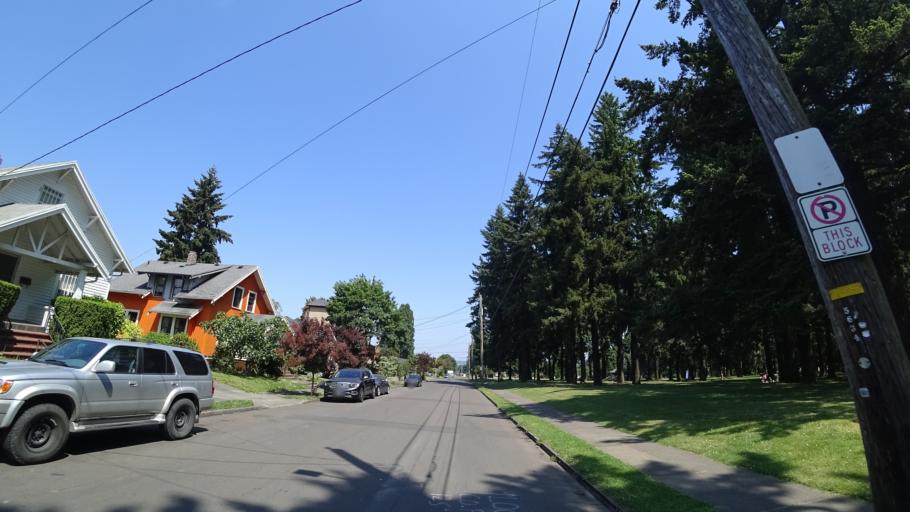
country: US
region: Oregon
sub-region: Multnomah County
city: Portland
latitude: 45.5637
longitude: -122.6460
